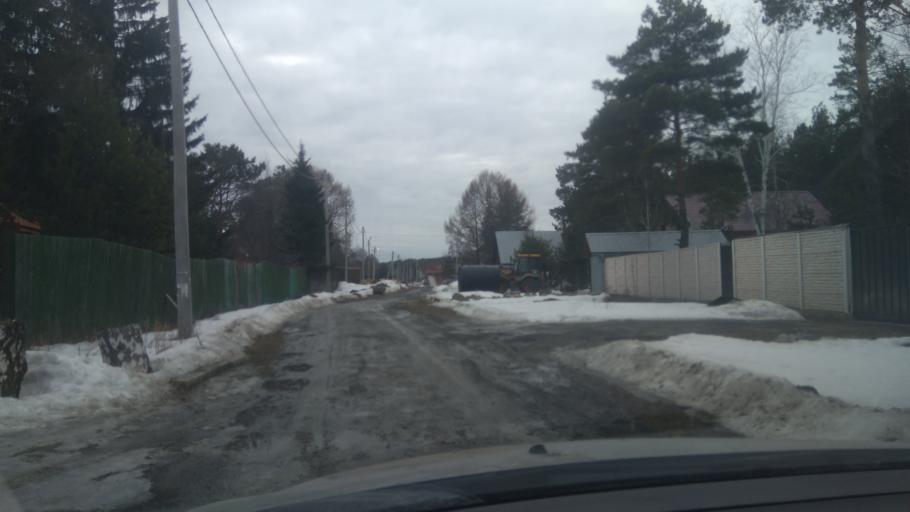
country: RU
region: Sverdlovsk
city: Severka
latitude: 56.8537
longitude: 60.3844
